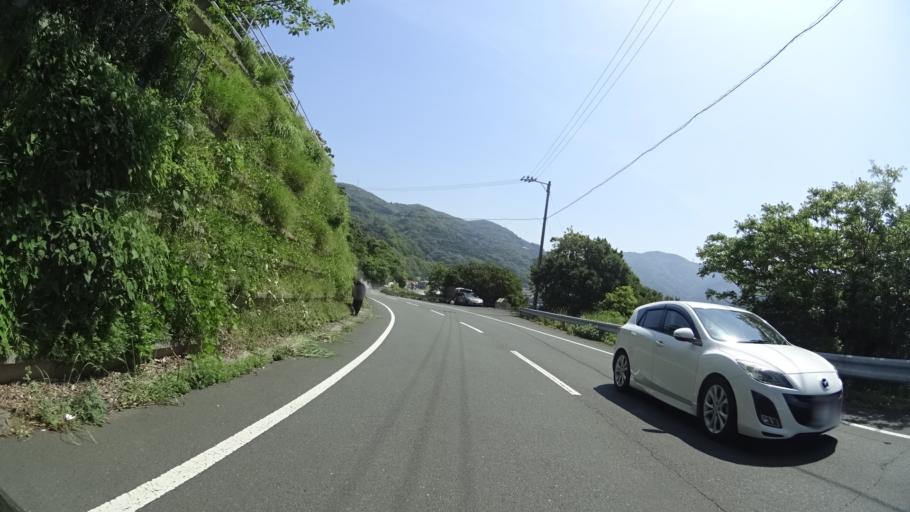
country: JP
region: Ehime
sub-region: Nishiuwa-gun
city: Ikata-cho
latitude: 33.3899
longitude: 132.1109
